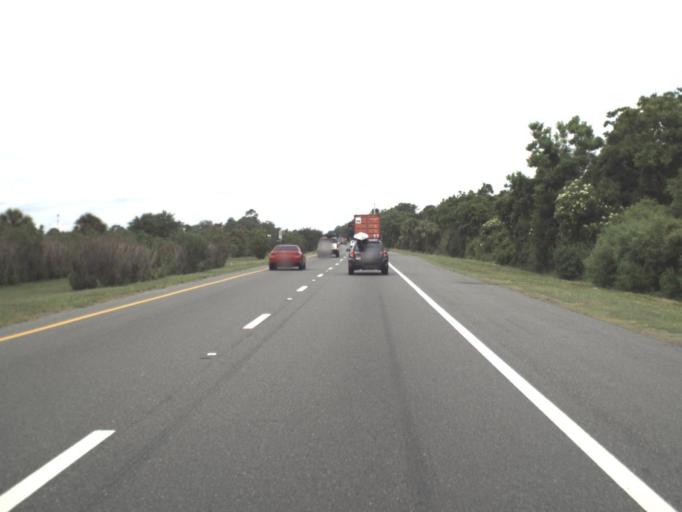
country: US
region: Florida
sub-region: Duval County
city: Jacksonville
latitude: 30.4122
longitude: -81.5515
